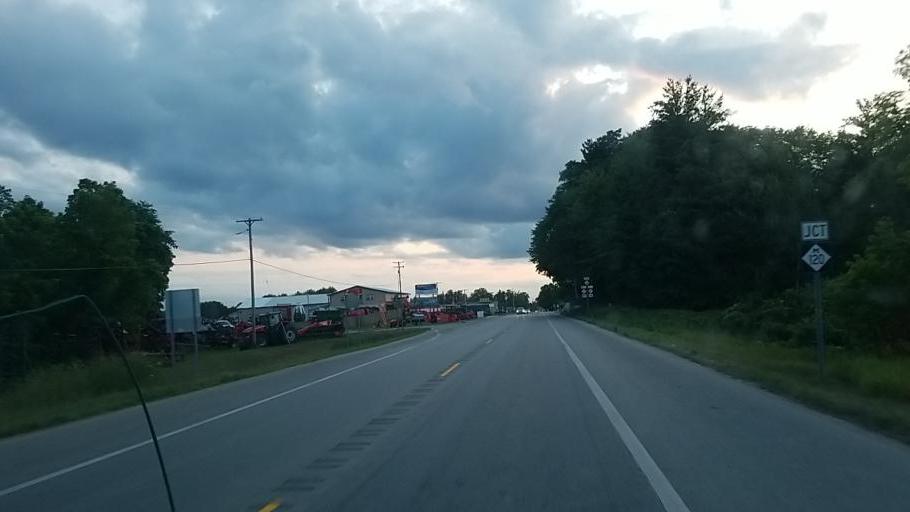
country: US
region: Michigan
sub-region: Newaygo County
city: Fremont
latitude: 43.4674
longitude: -86.0353
